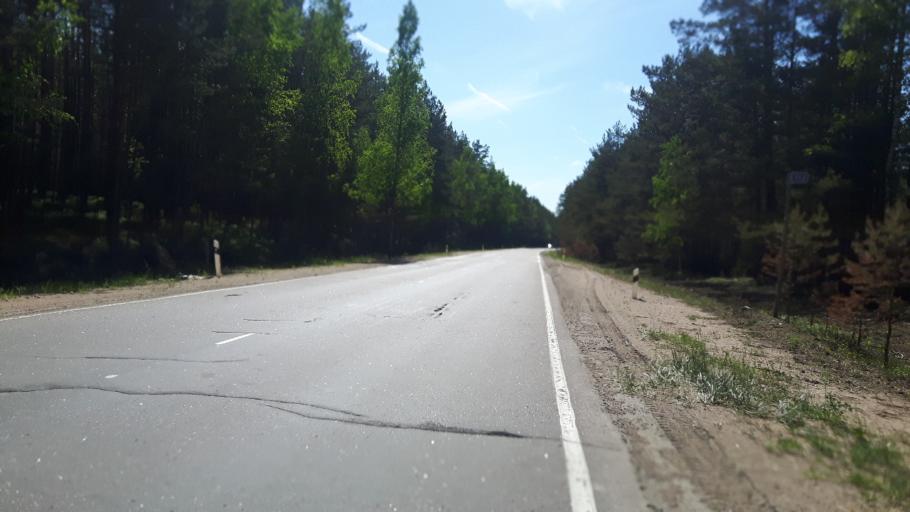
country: RU
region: Leningrad
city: Sista-Palkino
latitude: 59.7761
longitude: 28.8599
